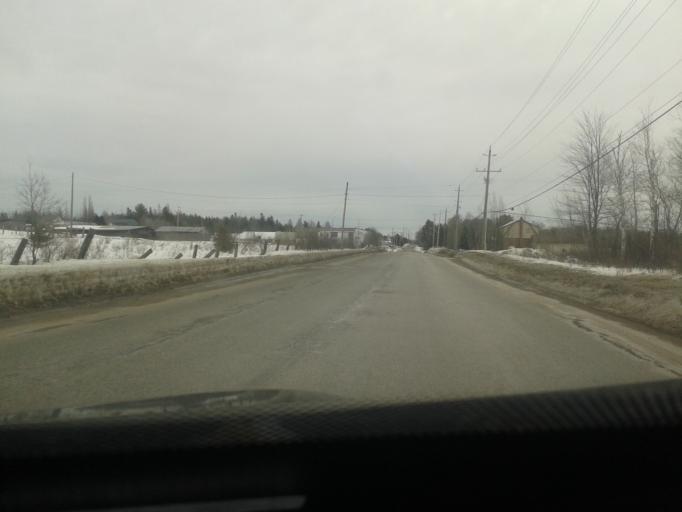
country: CA
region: Ontario
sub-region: Nipissing District
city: North Bay
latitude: 46.3471
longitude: -79.4745
